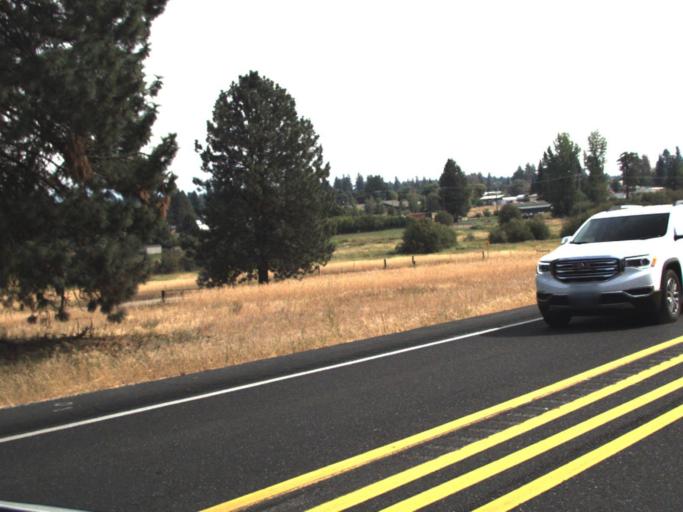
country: US
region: Washington
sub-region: Spokane County
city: Deer Park
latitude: 47.9553
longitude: -117.4895
